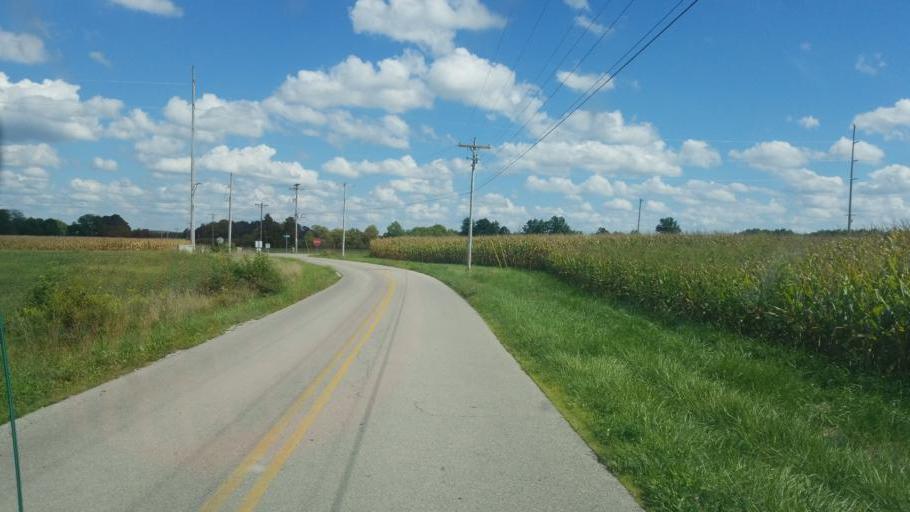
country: US
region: Ohio
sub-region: Delaware County
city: Delaware
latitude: 40.3098
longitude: -83.2004
